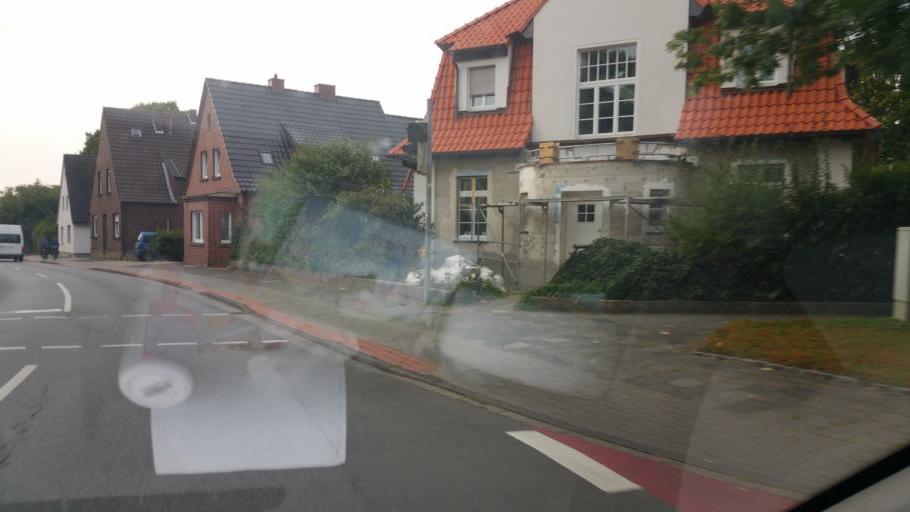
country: DE
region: North Rhine-Westphalia
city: Emsdetten
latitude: 52.1678
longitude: 7.5318
